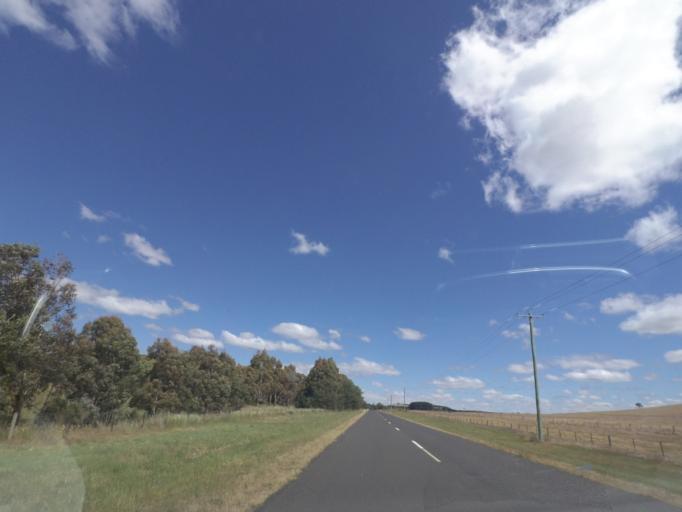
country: AU
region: Victoria
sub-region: Hume
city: Sunbury
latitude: -37.3120
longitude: 144.5182
